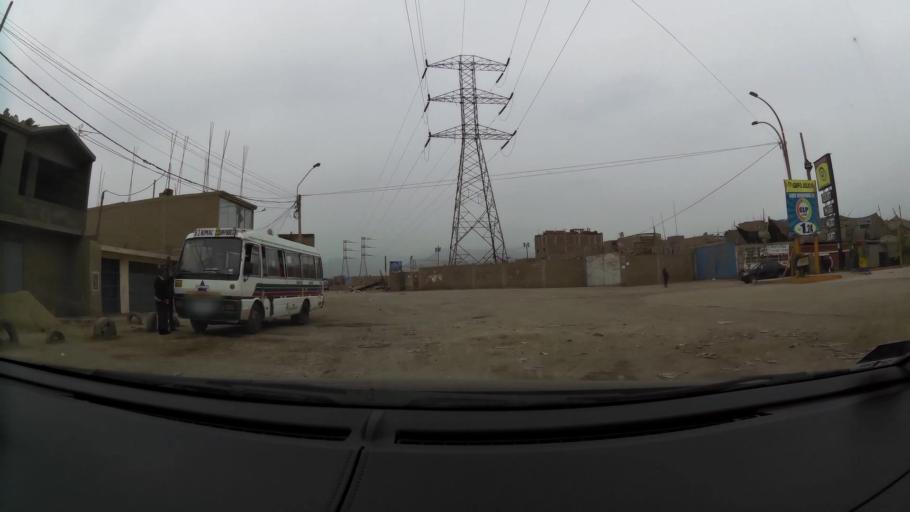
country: PE
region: Lima
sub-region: Lima
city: Independencia
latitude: -11.9560
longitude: -77.0879
